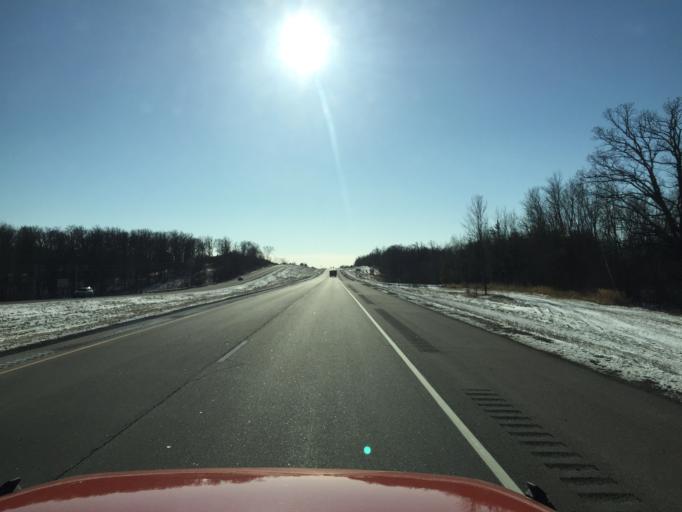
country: US
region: Minnesota
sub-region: Mille Lacs County
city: Milaca
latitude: 45.8158
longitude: -93.6554
